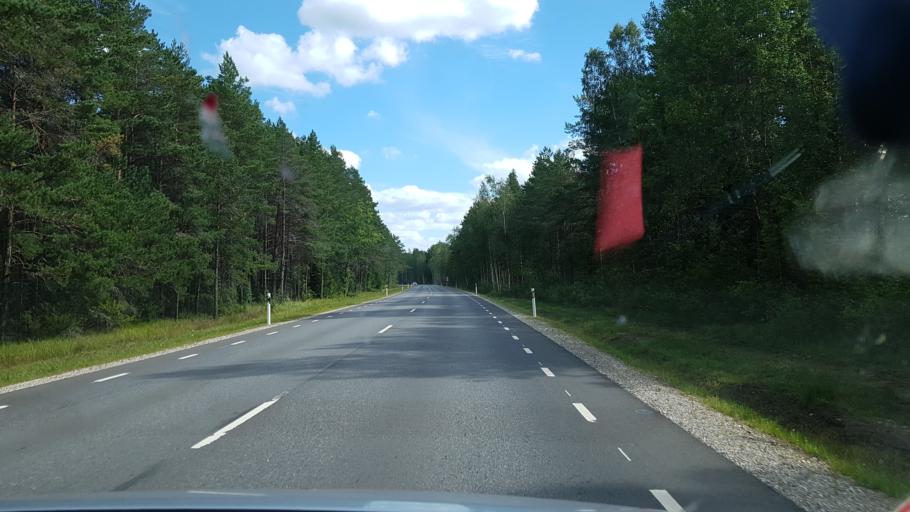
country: EE
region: Harju
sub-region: Nissi vald
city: Turba
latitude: 59.0868
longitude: 23.9460
